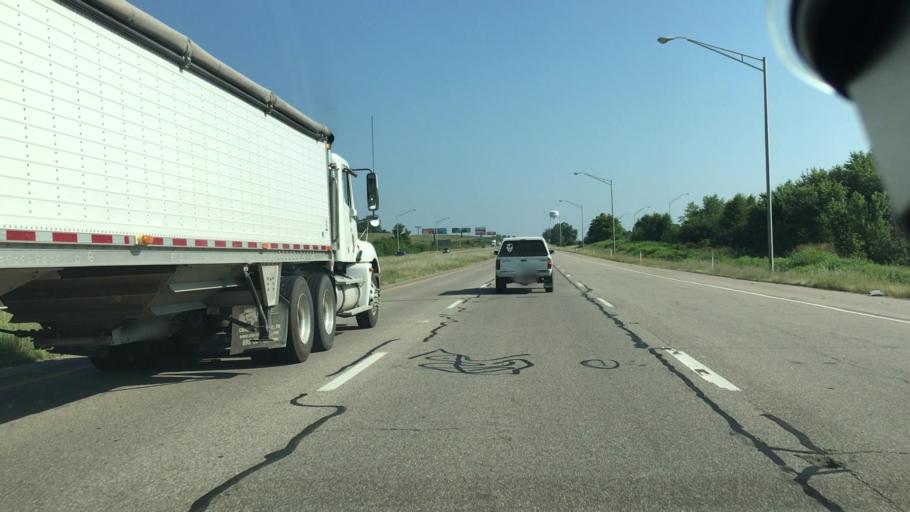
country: US
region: Indiana
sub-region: Gibson County
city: Fort Branch
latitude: 38.2781
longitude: -87.5676
